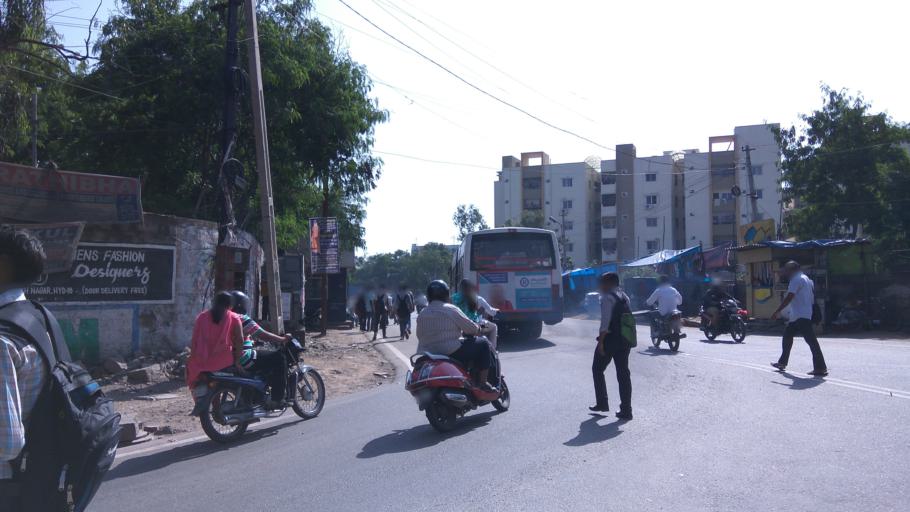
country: IN
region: Telangana
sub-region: Rangareddi
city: Kukatpalli
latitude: 17.4562
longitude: 78.4342
